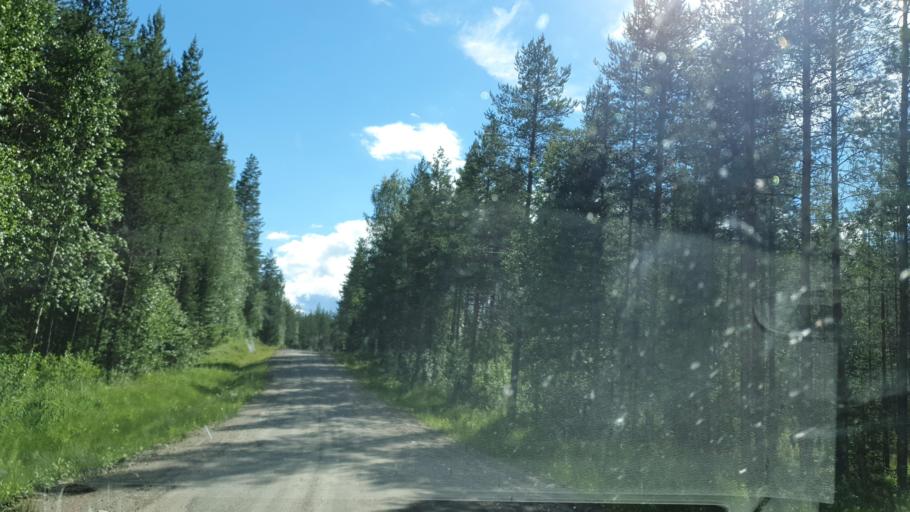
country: FI
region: Kainuu
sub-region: Kehys-Kainuu
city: Kuhmo
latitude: 64.1580
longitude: 29.8087
